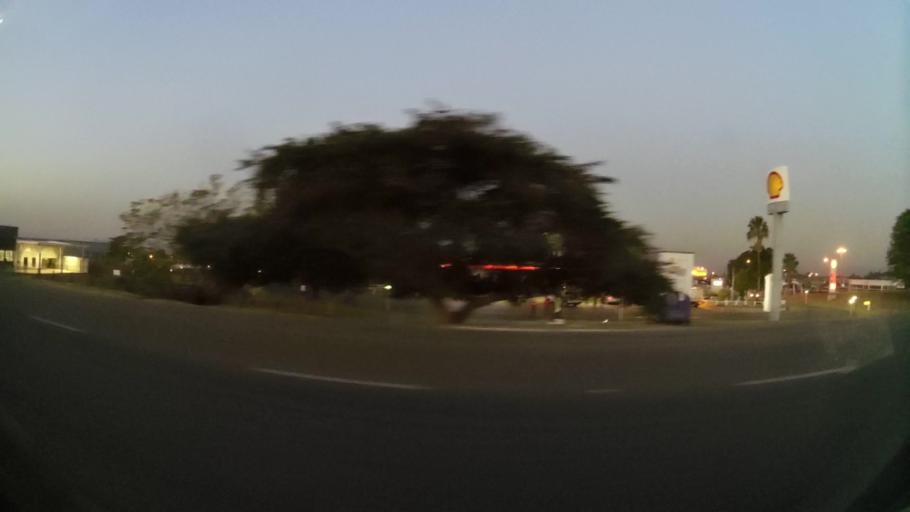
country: ZA
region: North-West
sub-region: Bojanala Platinum District Municipality
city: Rustenburg
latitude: -25.6881
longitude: 27.2537
